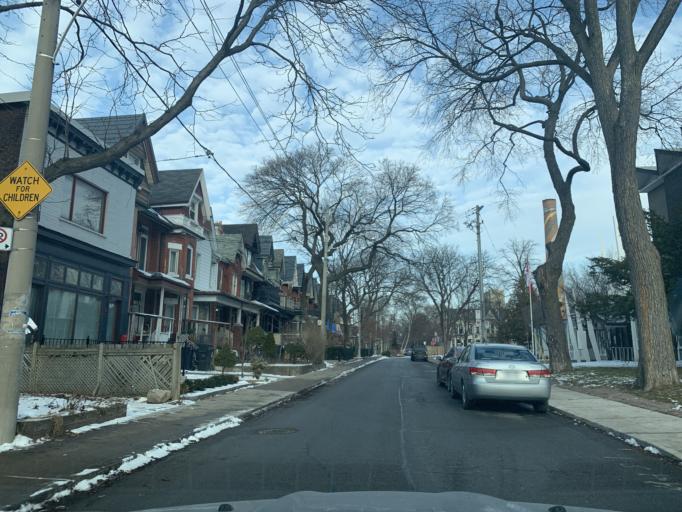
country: CA
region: Ontario
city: Toronto
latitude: 43.6585
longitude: -79.4021
